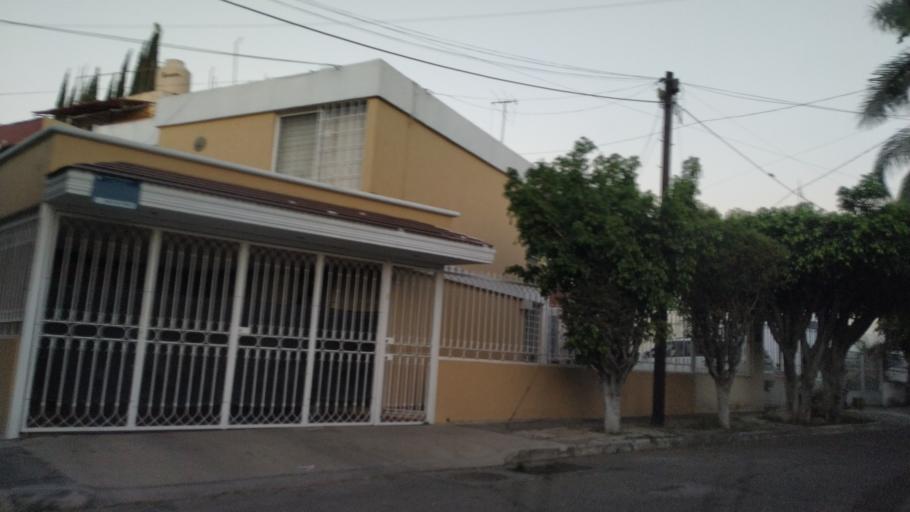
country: MX
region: Jalisco
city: Tlaquepaque
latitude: 20.6543
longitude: -103.3303
